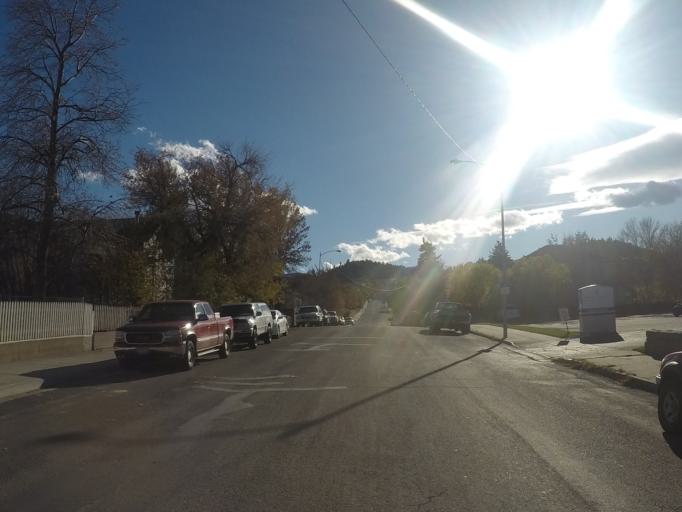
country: US
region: Montana
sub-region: Lewis and Clark County
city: Helena
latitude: 46.5844
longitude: -112.0359
